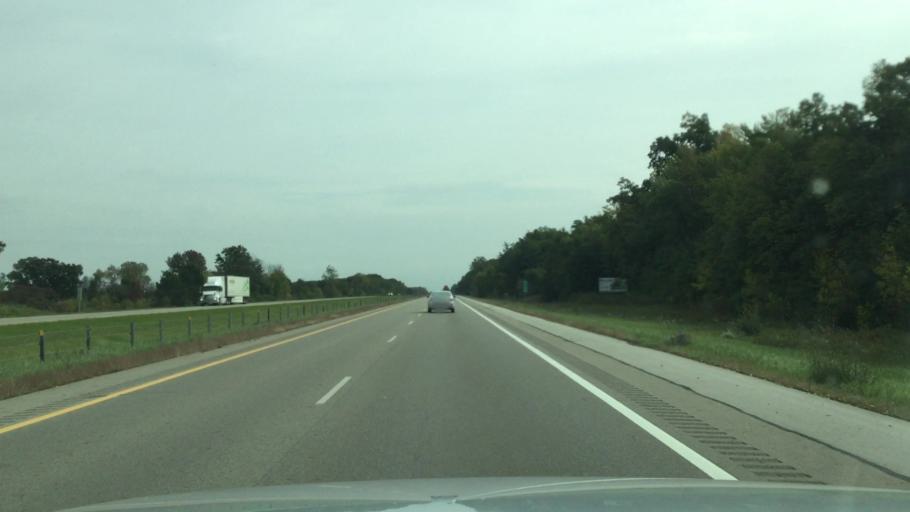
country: US
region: Michigan
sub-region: Genesee County
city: Swartz Creek
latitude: 42.9647
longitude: -83.8883
